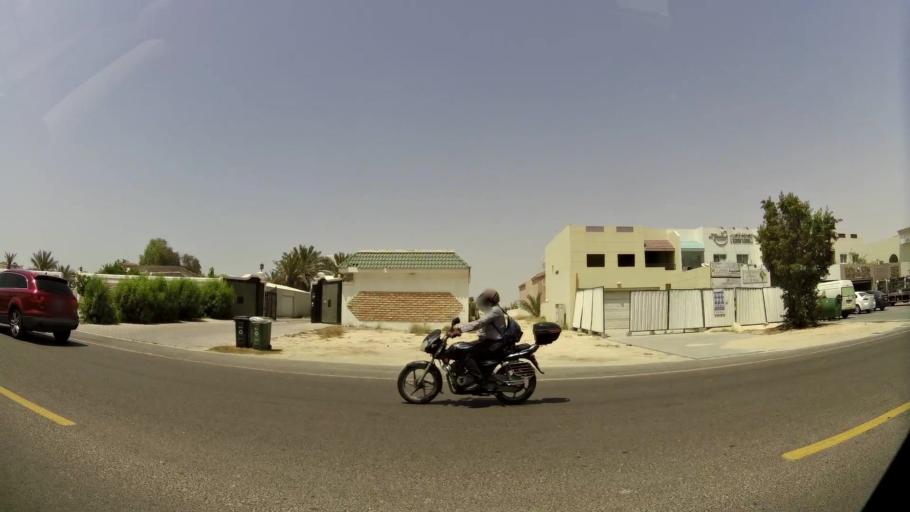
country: AE
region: Dubai
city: Dubai
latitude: 25.1437
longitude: 55.1992
